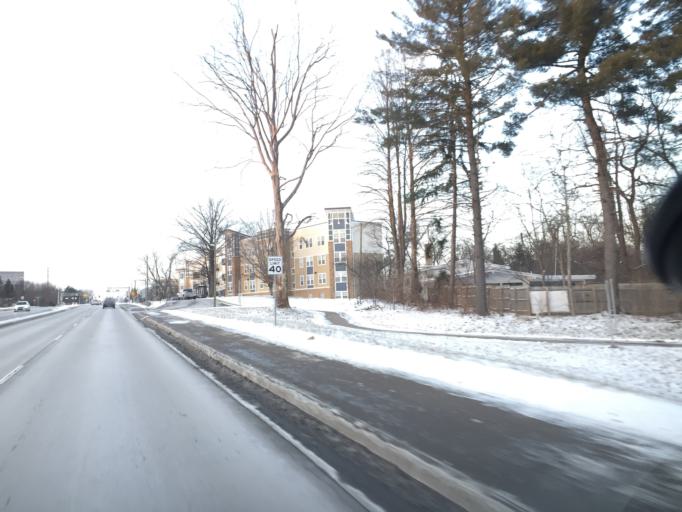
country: US
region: Indiana
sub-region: Monroe County
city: Bloomington
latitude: 39.1683
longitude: -86.5004
